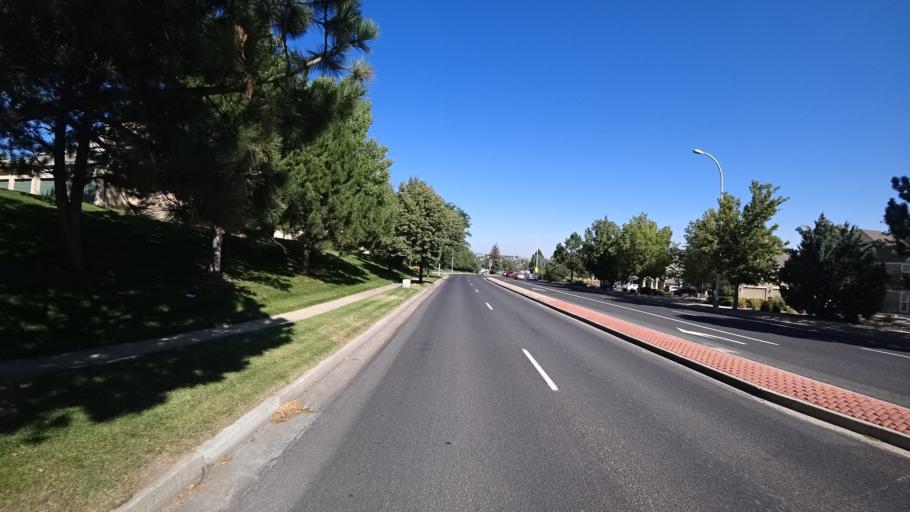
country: US
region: Colorado
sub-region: El Paso County
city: Cimarron Hills
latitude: 38.9252
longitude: -104.7506
